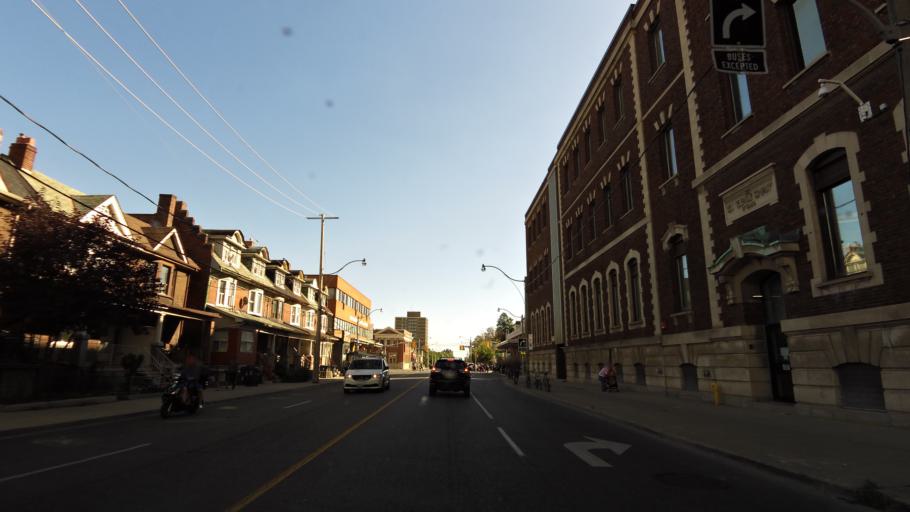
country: CA
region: Ontario
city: Toronto
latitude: 43.6607
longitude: -79.4357
